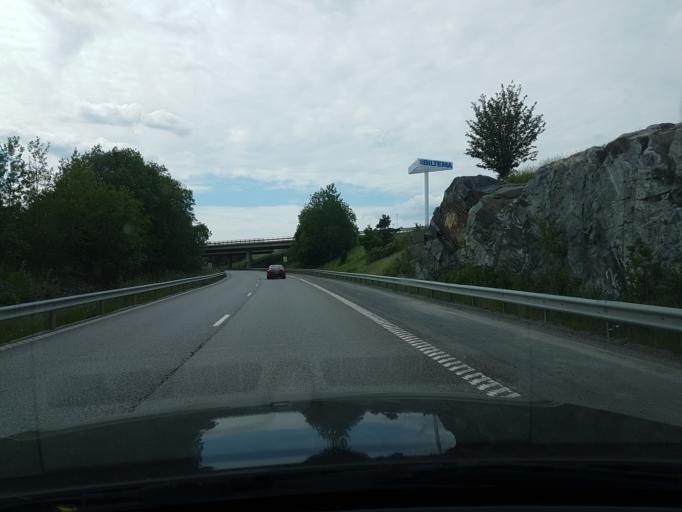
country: SE
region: Stockholm
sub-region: Norrtalje Kommun
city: Norrtalje
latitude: 59.7439
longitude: 18.6814
